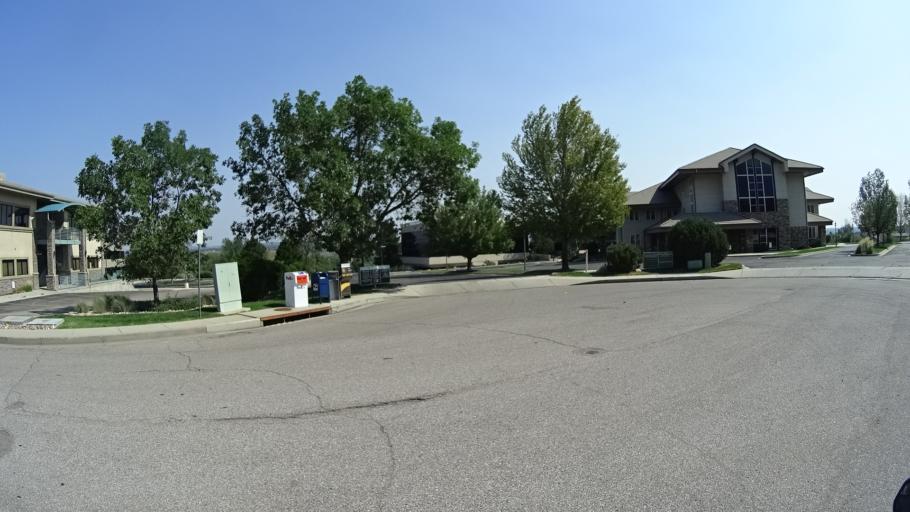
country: US
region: Colorado
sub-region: El Paso County
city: Colorado Springs
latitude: 38.7962
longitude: -104.8160
